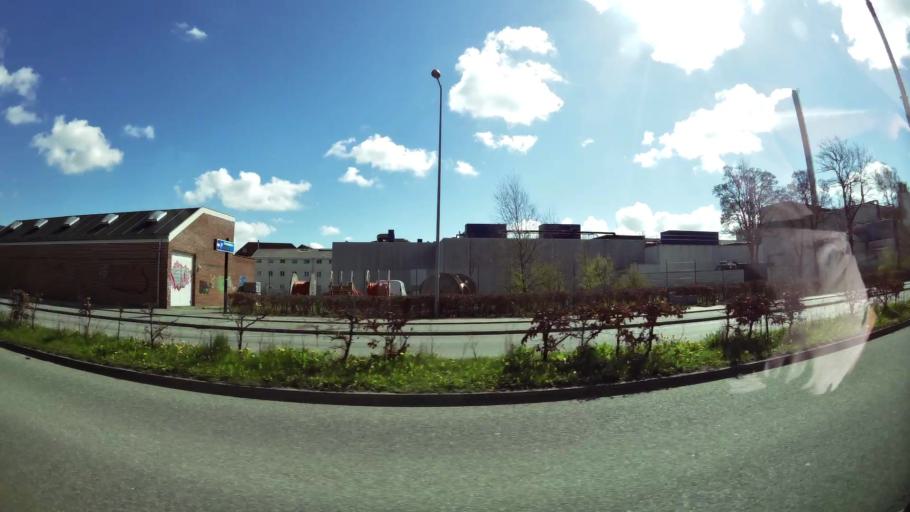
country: DK
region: North Denmark
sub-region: Alborg Kommune
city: Aalborg
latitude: 57.0451
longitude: 9.9343
